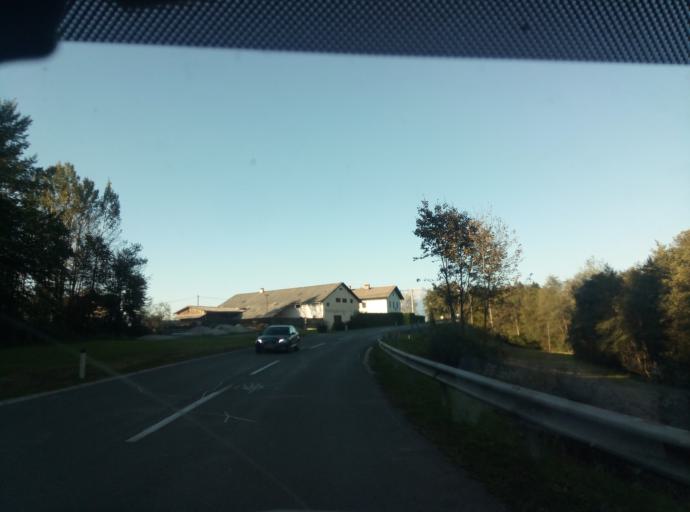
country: SI
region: Medvode
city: Zgornje Pirnice
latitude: 46.1403
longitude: 14.4784
